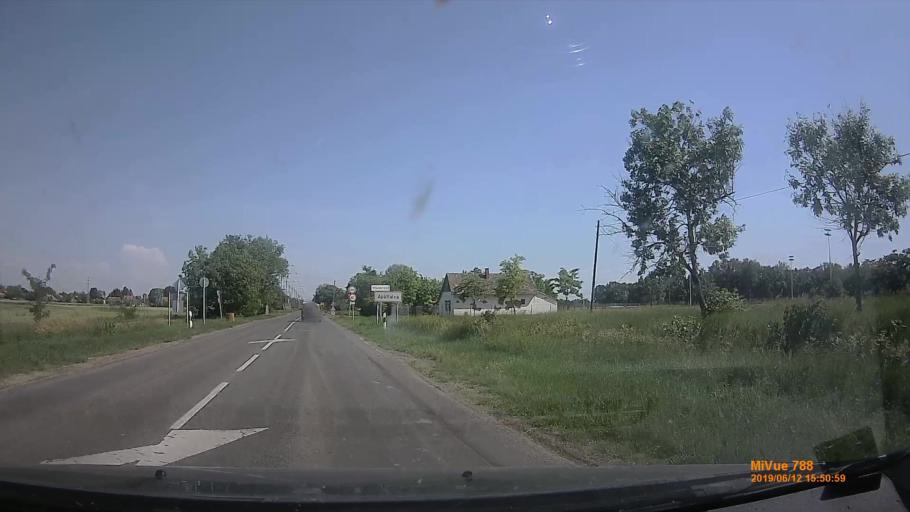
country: HU
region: Csongrad
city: Apatfalva
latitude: 46.1836
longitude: 20.5689
